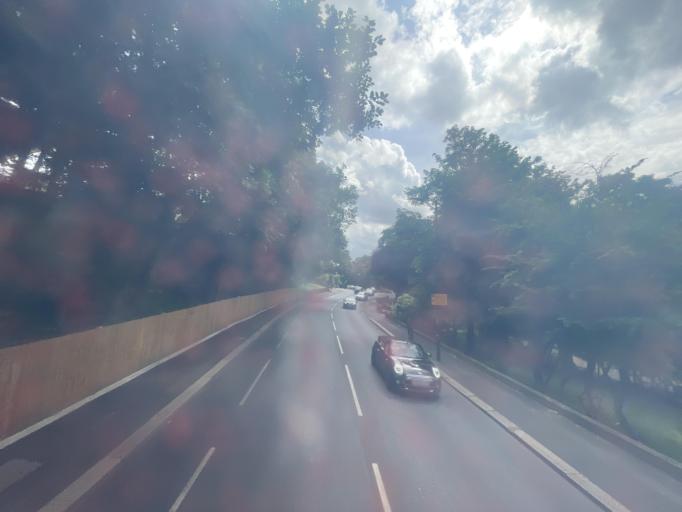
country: GB
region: England
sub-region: Greater London
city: Thornton Heath
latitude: 51.4252
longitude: -0.0761
